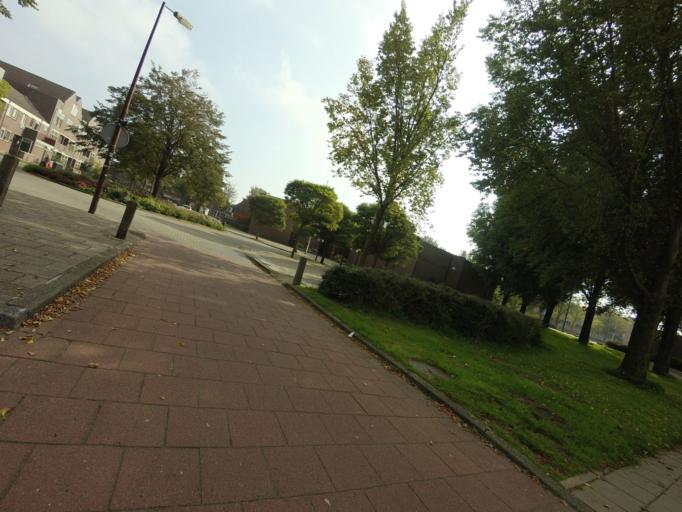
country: NL
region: North Holland
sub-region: Gemeente Alkmaar
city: Alkmaar
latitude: 52.6554
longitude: 4.7592
